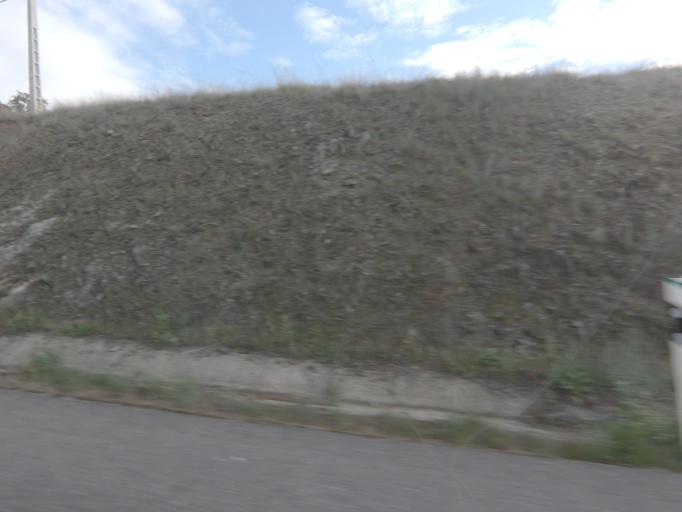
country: ES
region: Extremadura
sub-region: Provincia de Caceres
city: Canaveral
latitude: 39.8252
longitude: -6.3735
